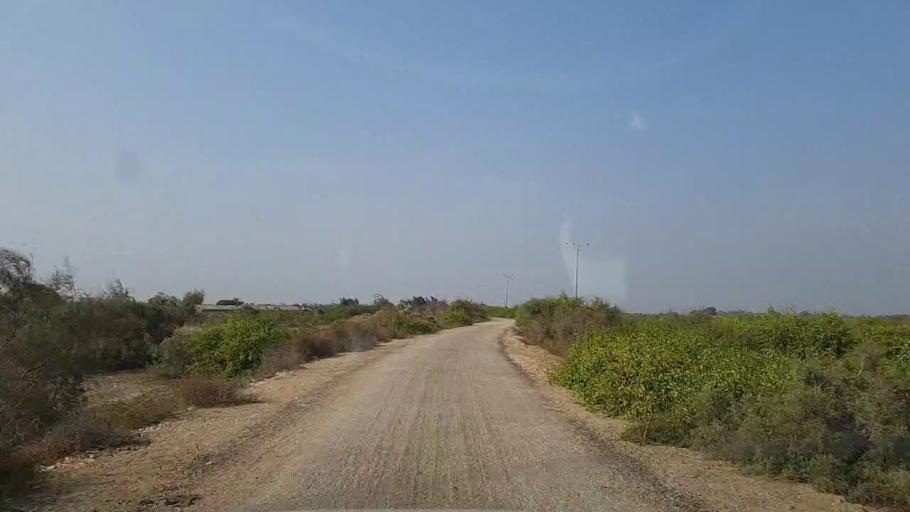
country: PK
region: Sindh
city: Mirpur Sakro
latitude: 24.5769
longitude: 67.5694
